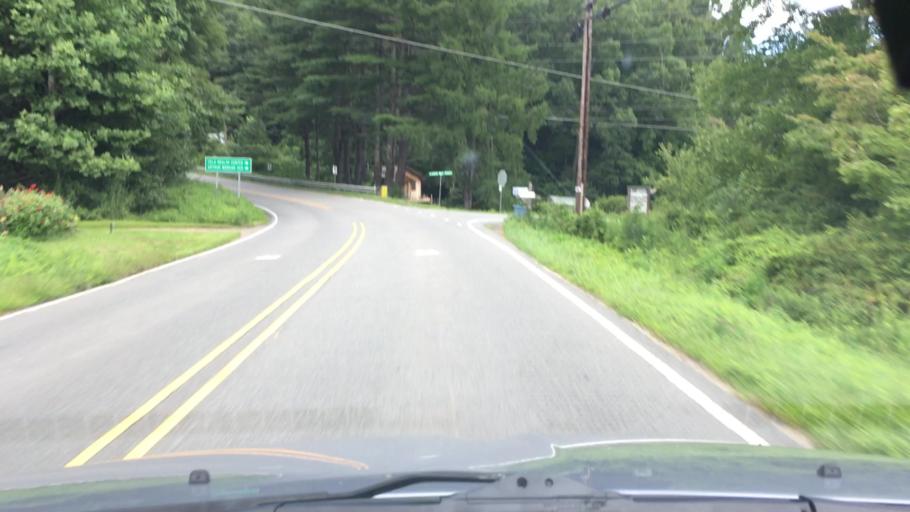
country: US
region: North Carolina
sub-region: Yancey County
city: Burnsville
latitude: 35.8326
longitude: -82.1847
